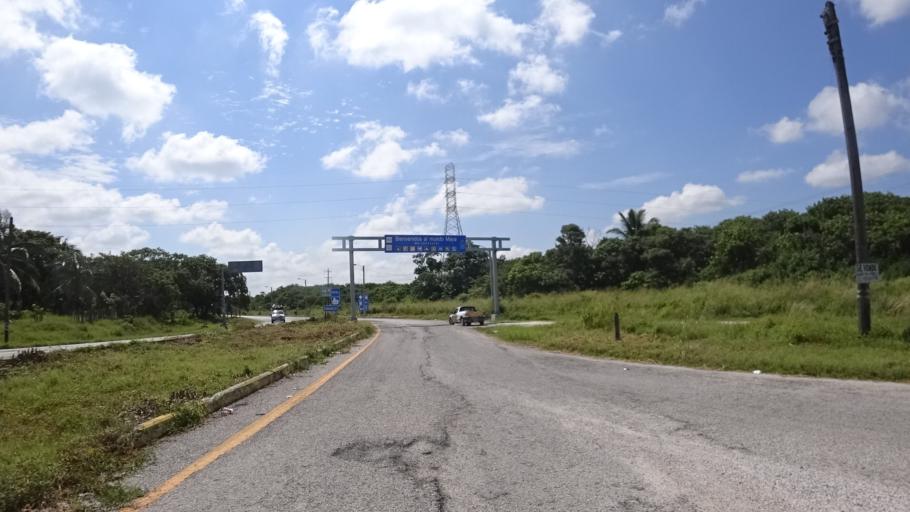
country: MX
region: Campeche
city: Sabancuy
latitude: 18.9896
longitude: -91.1912
